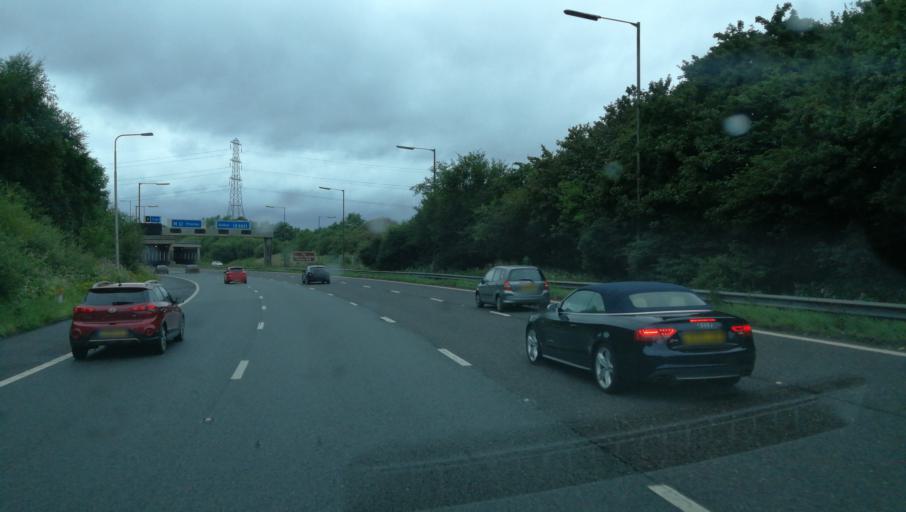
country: GB
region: England
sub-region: Borough of Bolton
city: Kearsley
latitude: 53.5277
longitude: -2.3647
